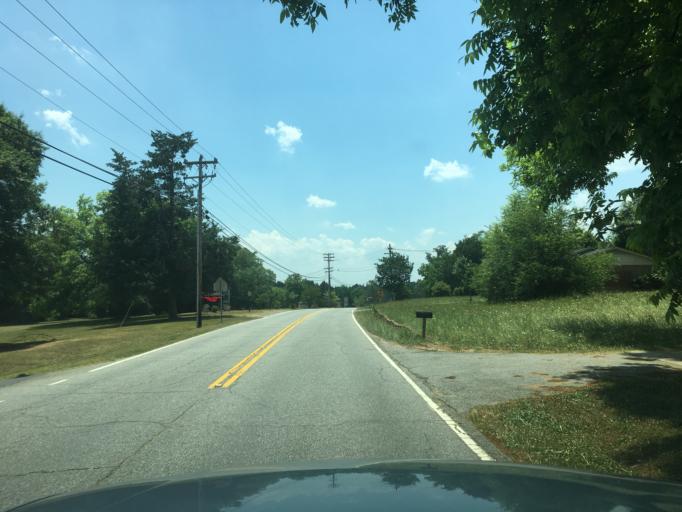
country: US
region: South Carolina
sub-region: Anderson County
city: Anderson
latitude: 34.5234
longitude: -82.6270
